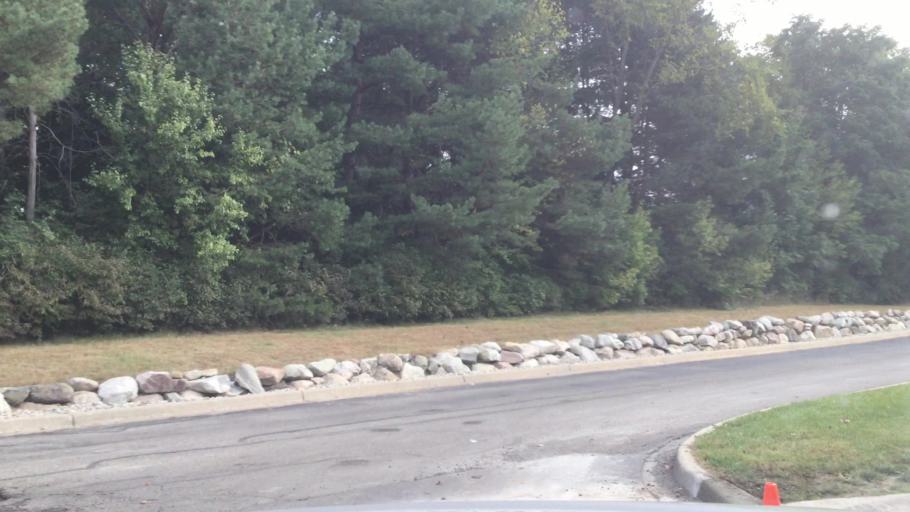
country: US
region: Michigan
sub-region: Genesee County
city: Flushing
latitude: 43.0565
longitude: -83.7742
